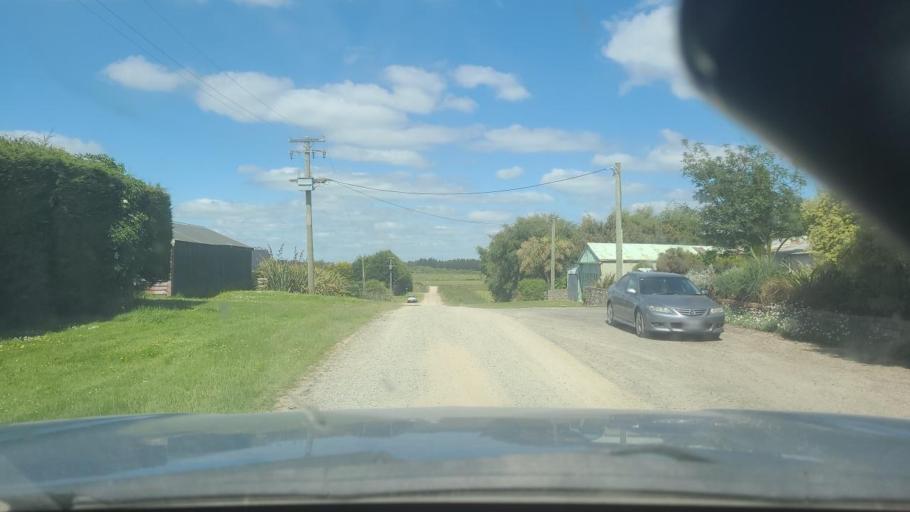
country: NZ
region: Southland
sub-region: Invercargill City
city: Invercargill
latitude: -46.3402
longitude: 168.2861
